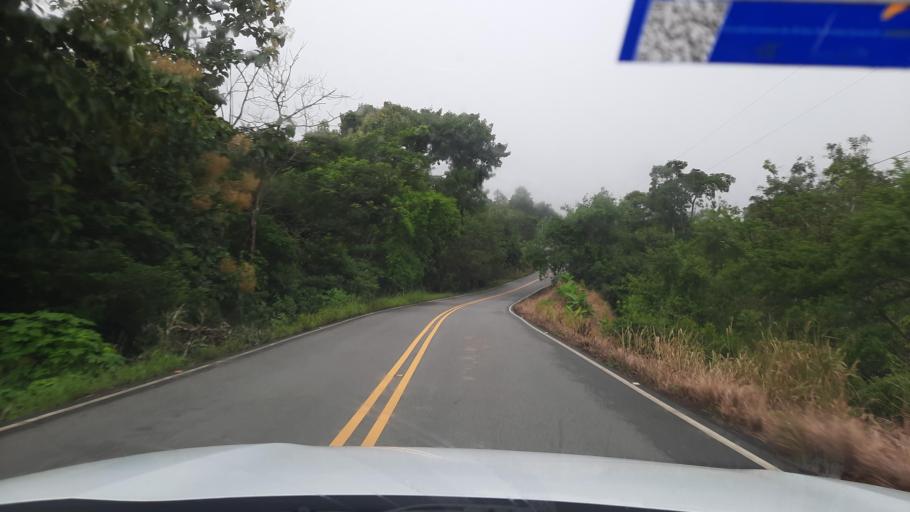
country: CR
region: Puntarenas
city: San Vito
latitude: 8.9362
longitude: -83.0964
